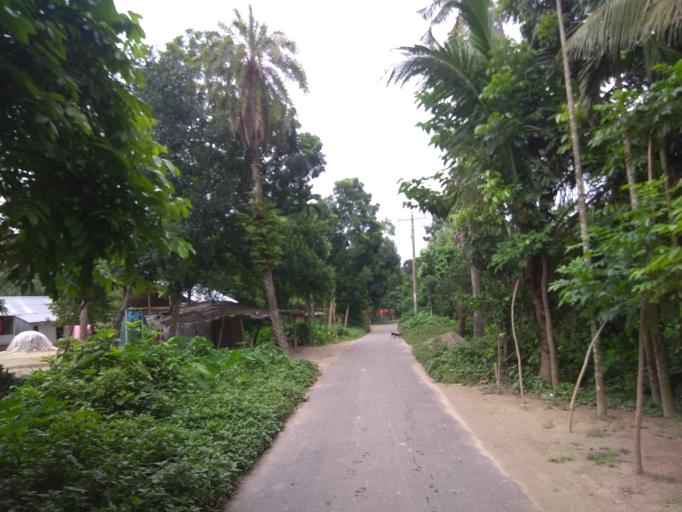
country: BD
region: Dhaka
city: Dohar
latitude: 23.4887
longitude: 89.9871
